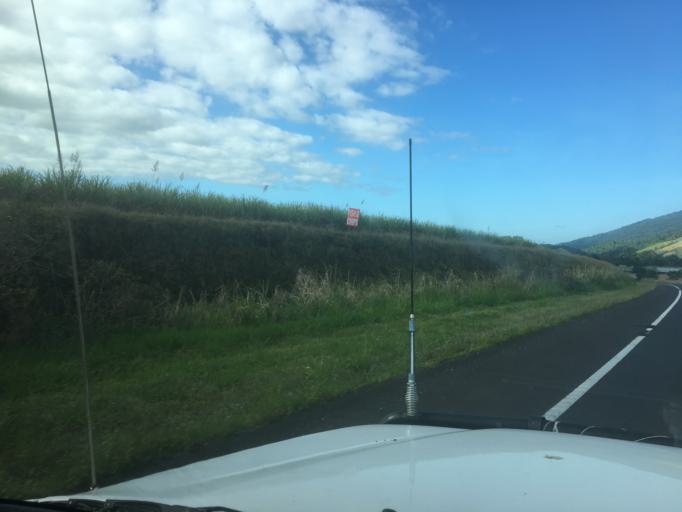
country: AU
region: Queensland
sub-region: Cassowary Coast
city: Innisfail
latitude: -17.2655
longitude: 145.9195
